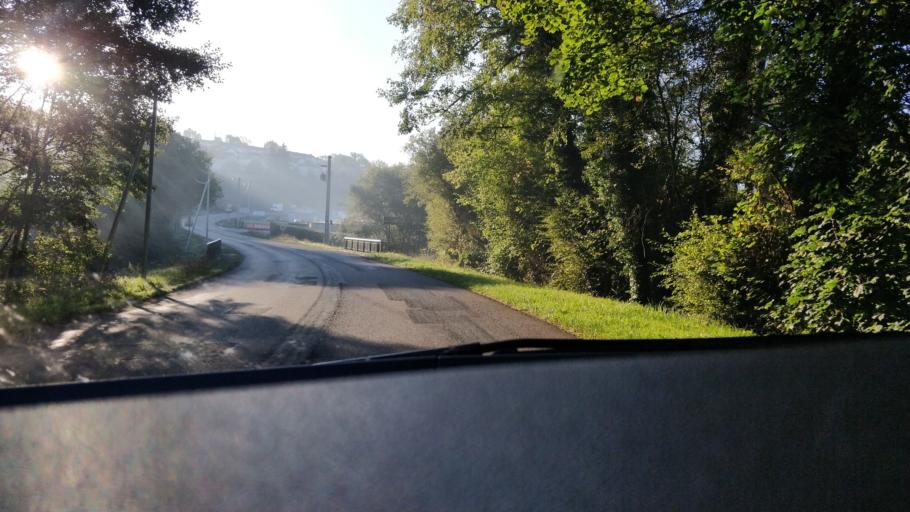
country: FR
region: Limousin
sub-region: Departement de la Creuse
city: Bourganeuf
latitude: 45.9560
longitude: 1.7414
